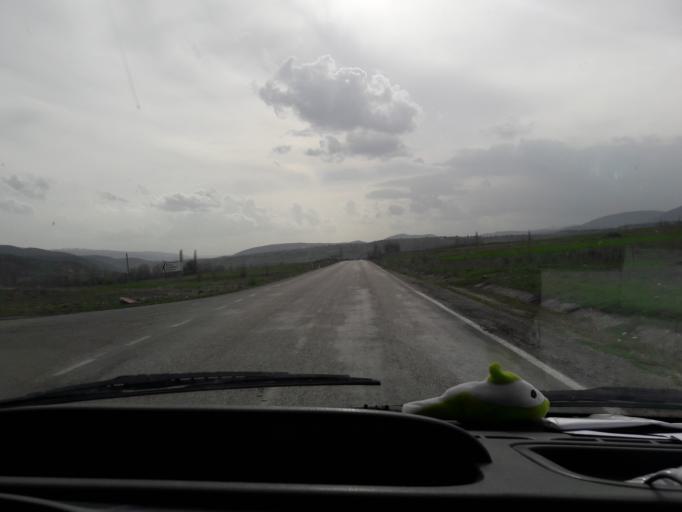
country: TR
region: Gumushane
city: Siran
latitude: 40.1617
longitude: 39.0315
